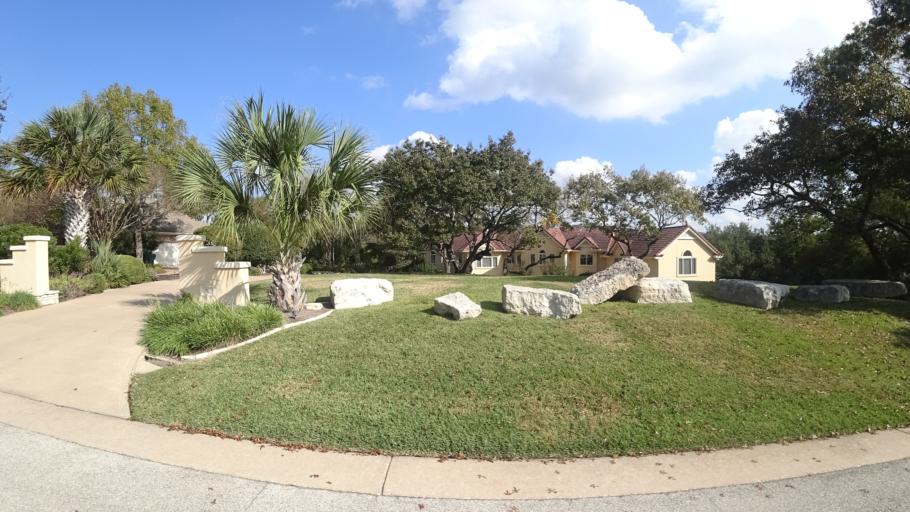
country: US
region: Texas
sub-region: Travis County
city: Lost Creek
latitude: 30.3028
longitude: -97.8507
